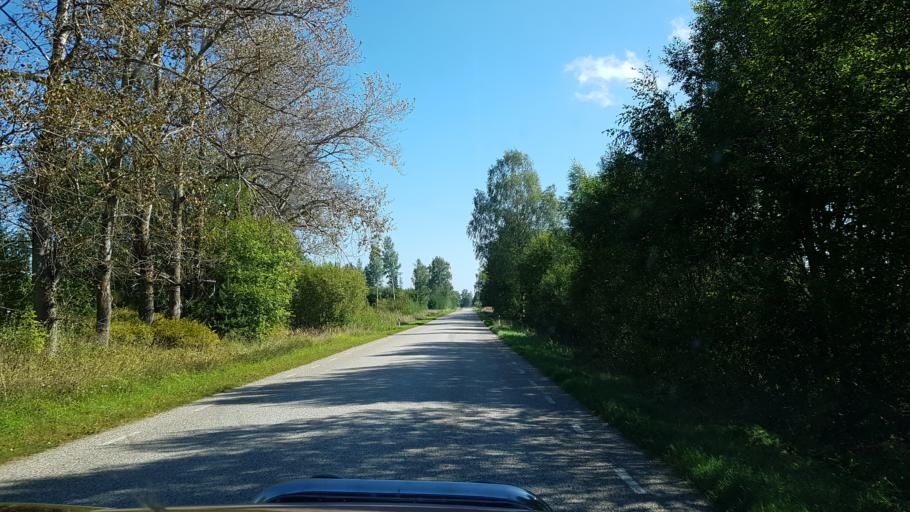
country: EE
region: Polvamaa
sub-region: Raepina vald
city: Rapina
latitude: 58.2294
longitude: 27.3871
